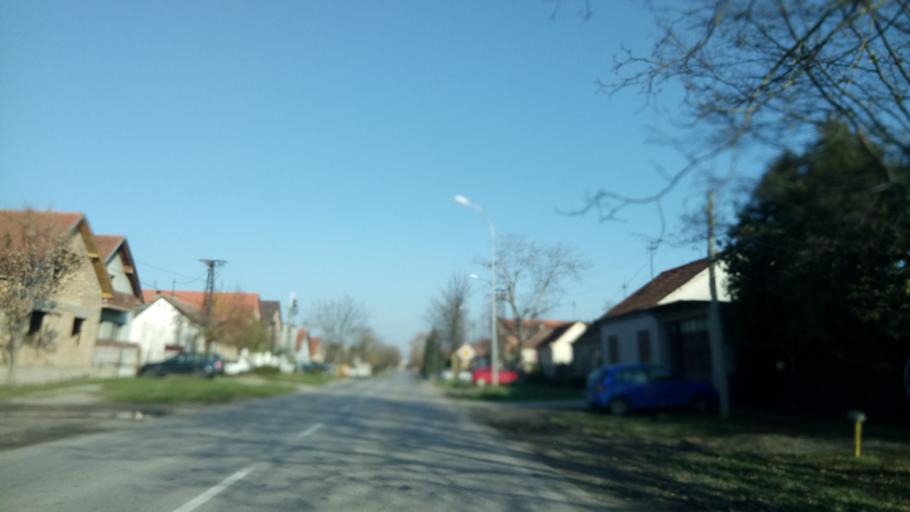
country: RS
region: Autonomna Pokrajina Vojvodina
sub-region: Sremski Okrug
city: Ingija
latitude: 45.0379
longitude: 20.0644
